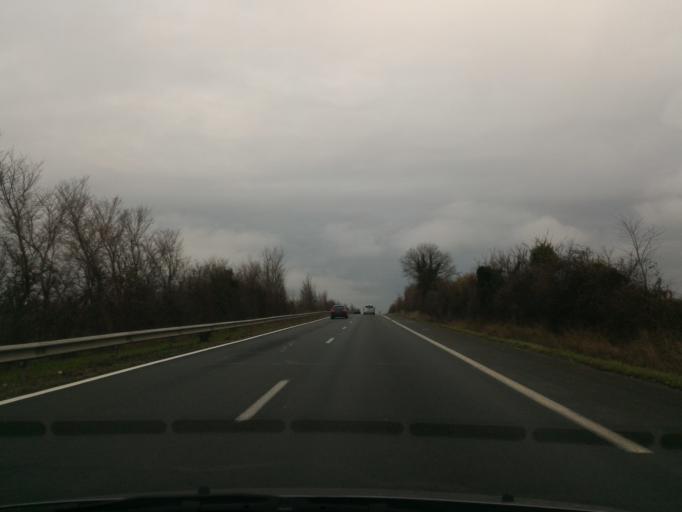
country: FR
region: Poitou-Charentes
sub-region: Departement de la Vienne
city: Vivonne
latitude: 46.4428
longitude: 0.2654
